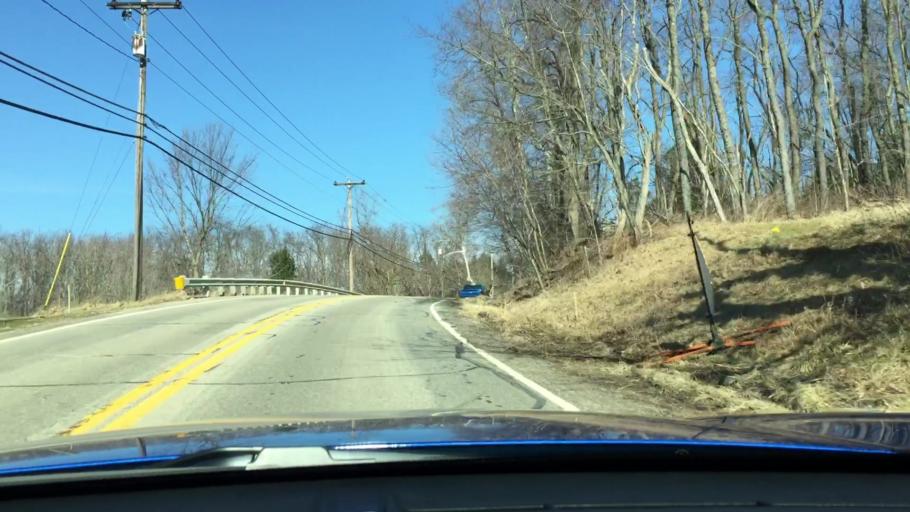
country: US
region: Pennsylvania
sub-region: Washington County
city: Cecil-Bishop
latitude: 40.3031
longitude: -80.1529
